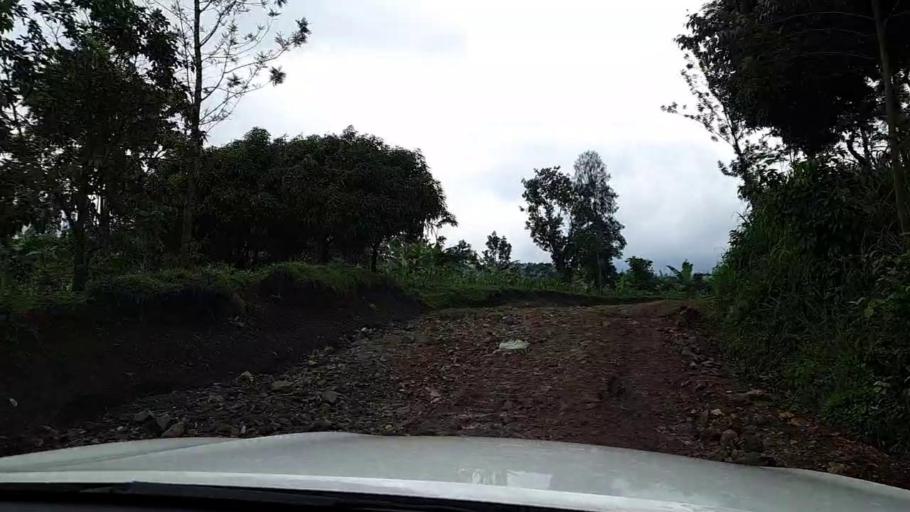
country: RW
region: Western Province
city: Cyangugu
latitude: -2.5619
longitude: 29.0360
